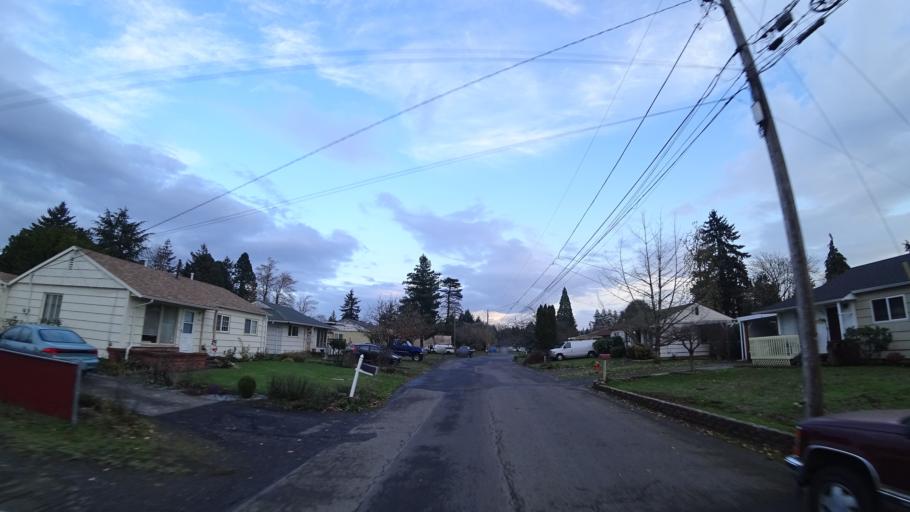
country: US
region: Oregon
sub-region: Multnomah County
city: Lents
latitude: 45.5286
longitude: -122.5363
